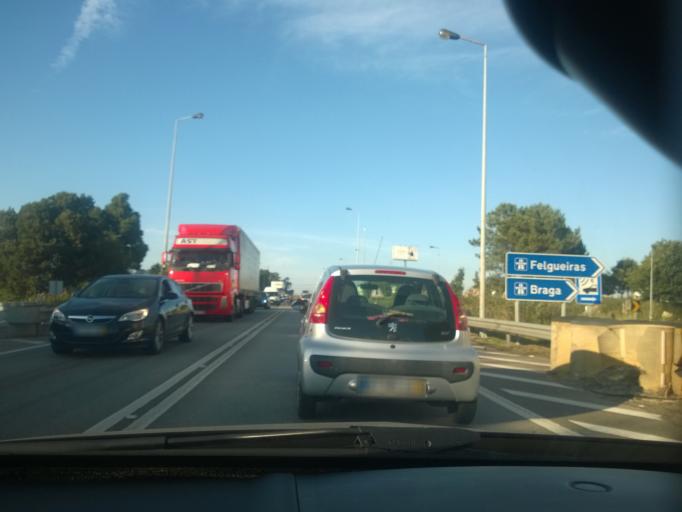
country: PT
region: Porto
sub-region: Maia
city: Maia
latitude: 41.2401
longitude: -8.6242
